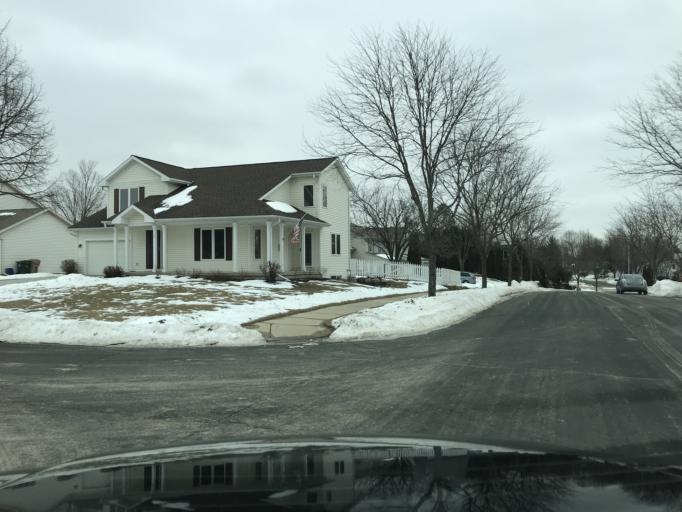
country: US
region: Wisconsin
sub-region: Dane County
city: Monona
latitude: 43.0721
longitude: -89.2839
